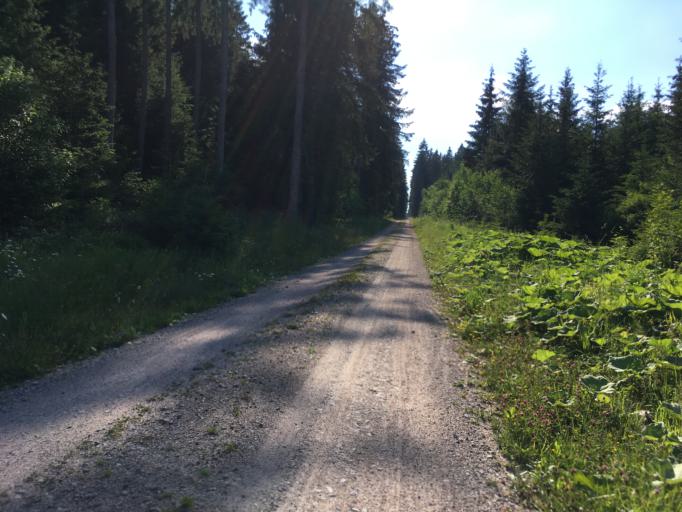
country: DE
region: Baden-Wuerttemberg
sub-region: Freiburg Region
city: Eisenbach
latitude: 47.9353
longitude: 8.3149
